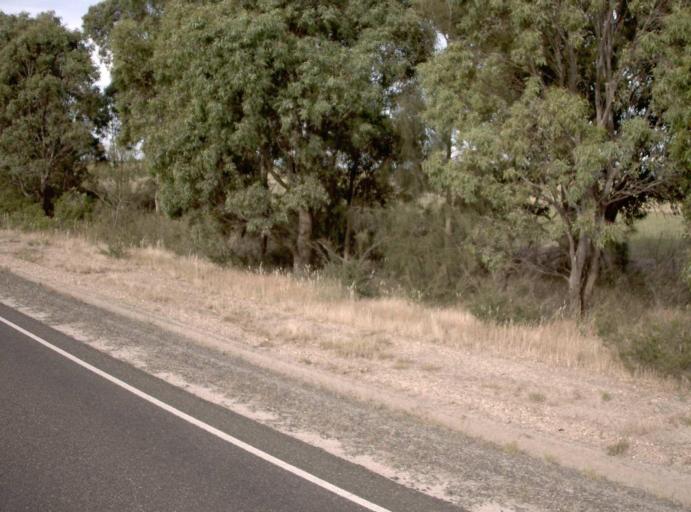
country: AU
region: Victoria
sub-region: Wellington
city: Heyfield
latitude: -38.0472
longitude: 146.6645
